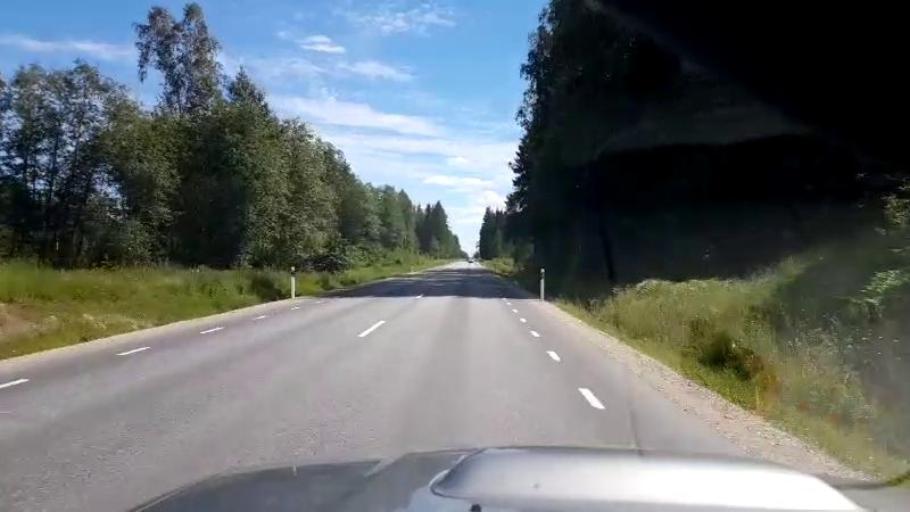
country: EE
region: Jogevamaa
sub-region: Jogeva linn
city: Jogeva
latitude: 58.7849
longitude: 26.3153
